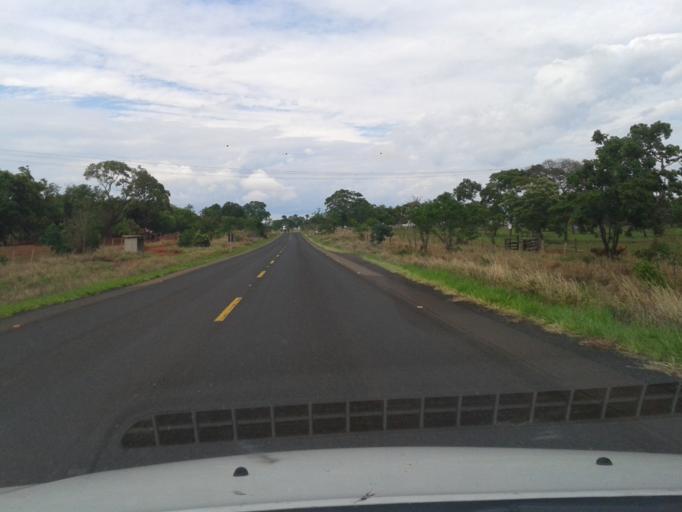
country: BR
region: Minas Gerais
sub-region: Campina Verde
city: Campina Verde
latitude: -19.5351
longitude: -49.7777
